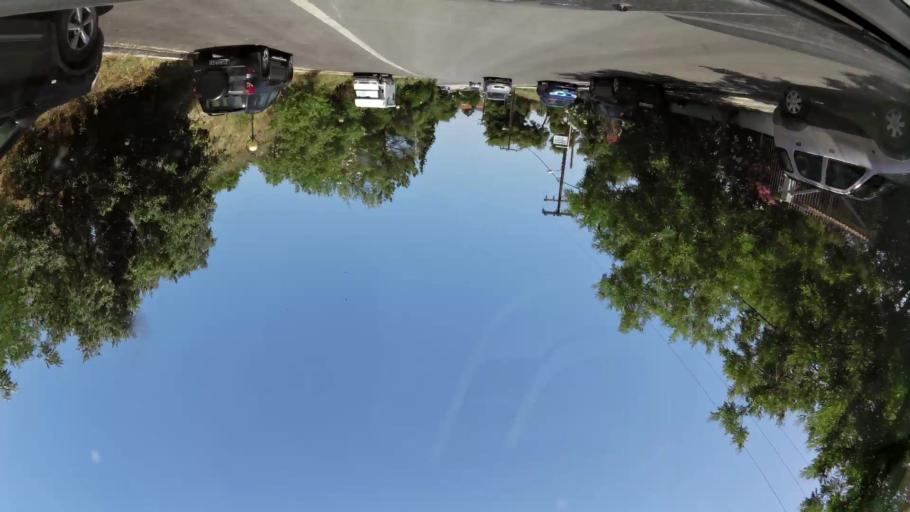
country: GR
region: Central Macedonia
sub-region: Nomos Thessalonikis
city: Trilofos
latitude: 40.4713
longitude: 22.9696
